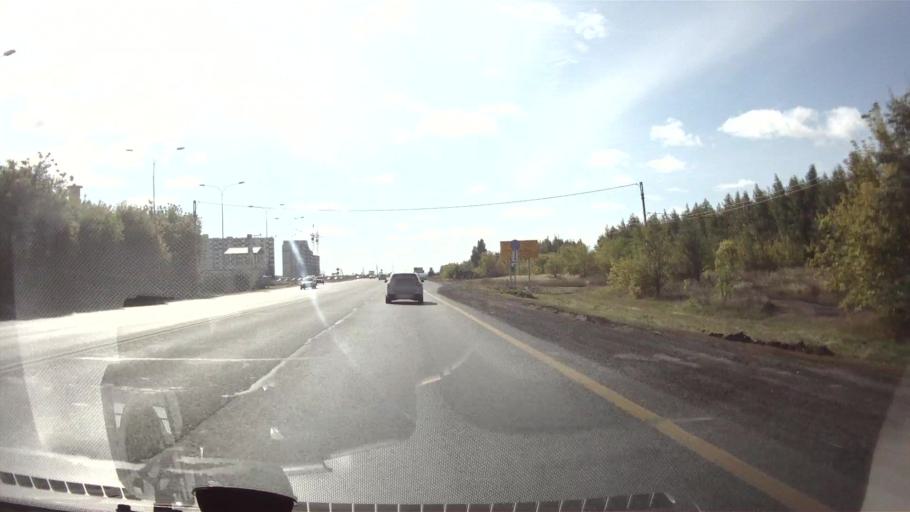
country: RU
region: Ulyanovsk
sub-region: Ulyanovskiy Rayon
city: Ulyanovsk
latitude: 54.2873
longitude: 48.2561
